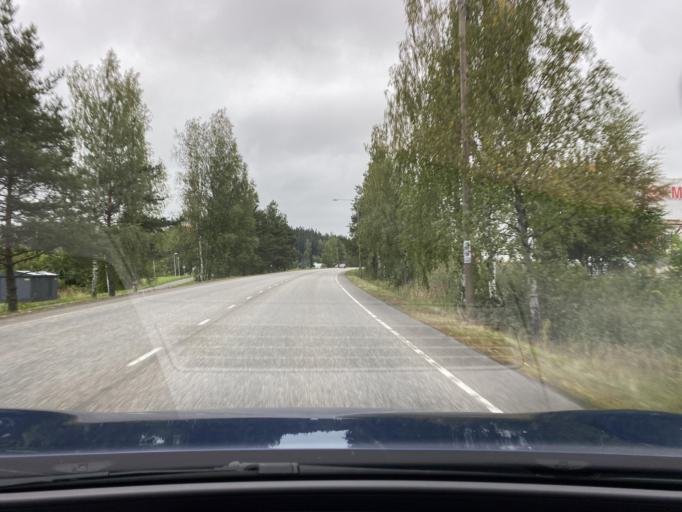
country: FI
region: Kymenlaakso
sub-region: Kouvola
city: Kouvola
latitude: 60.9021
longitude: 26.6073
